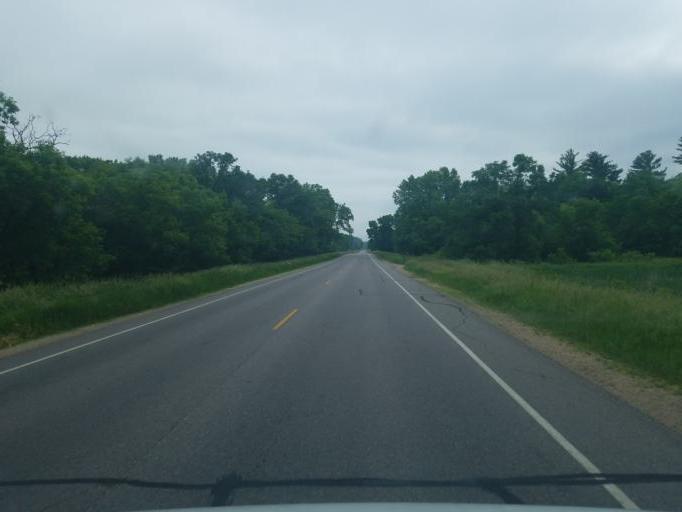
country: US
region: Wisconsin
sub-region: Juneau County
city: Elroy
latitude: 43.7039
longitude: -90.2664
